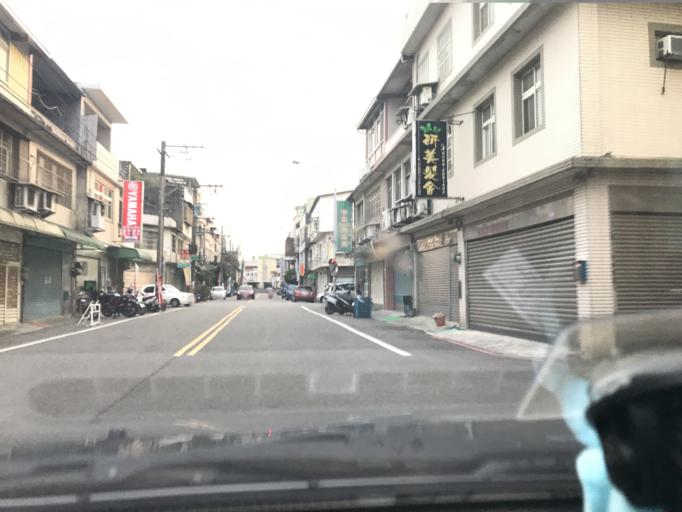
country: TW
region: Taiwan
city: Daxi
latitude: 24.8601
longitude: 121.2201
